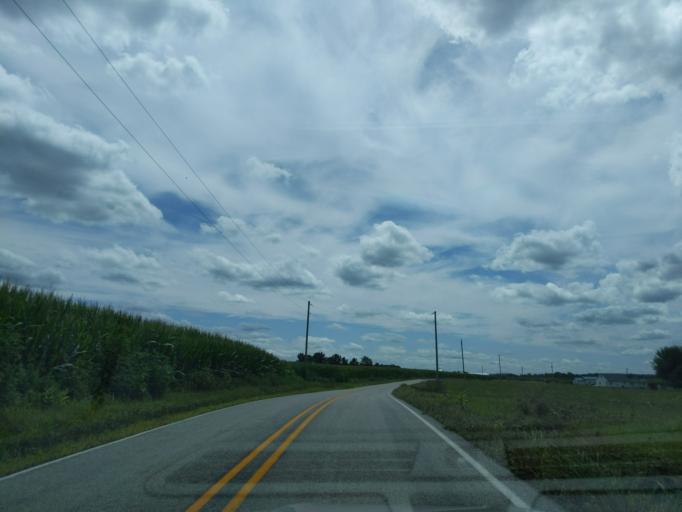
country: US
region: Indiana
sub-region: Ripley County
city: Osgood
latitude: 39.2082
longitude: -85.2758
